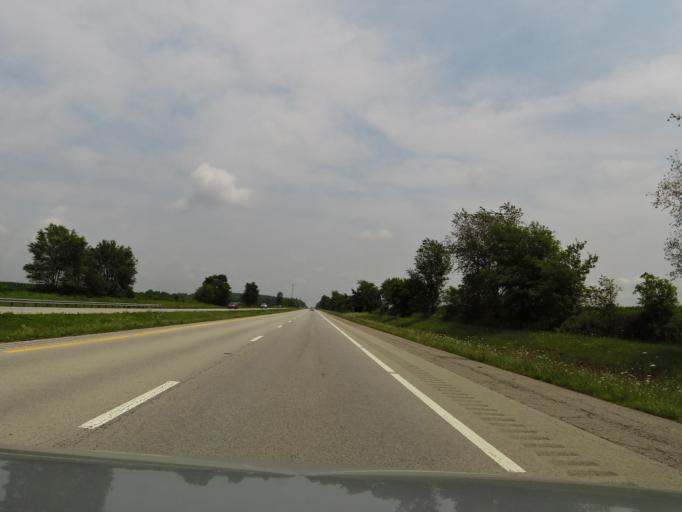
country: US
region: Kentucky
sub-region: Hardin County
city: Elizabethtown
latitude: 37.6050
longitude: -85.9778
